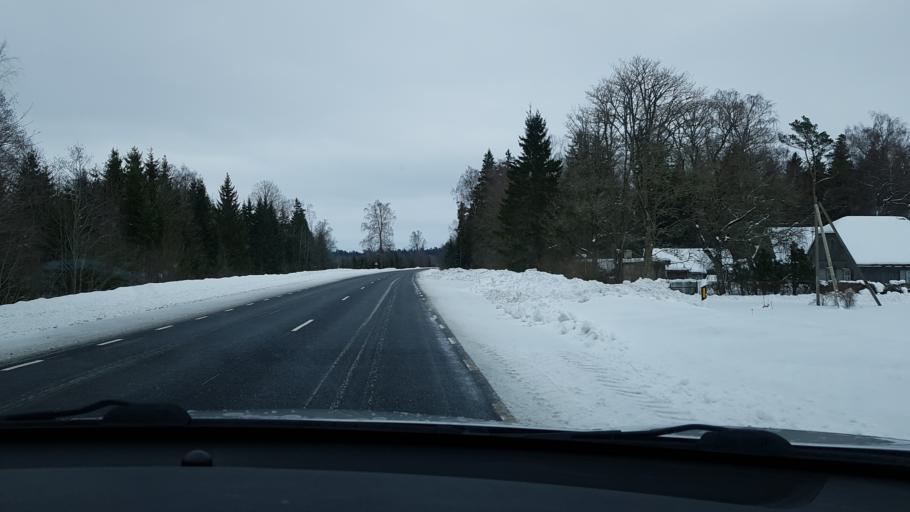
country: EE
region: Jaervamaa
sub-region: Jaerva-Jaani vald
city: Jarva-Jaani
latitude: 59.1052
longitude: 25.8089
